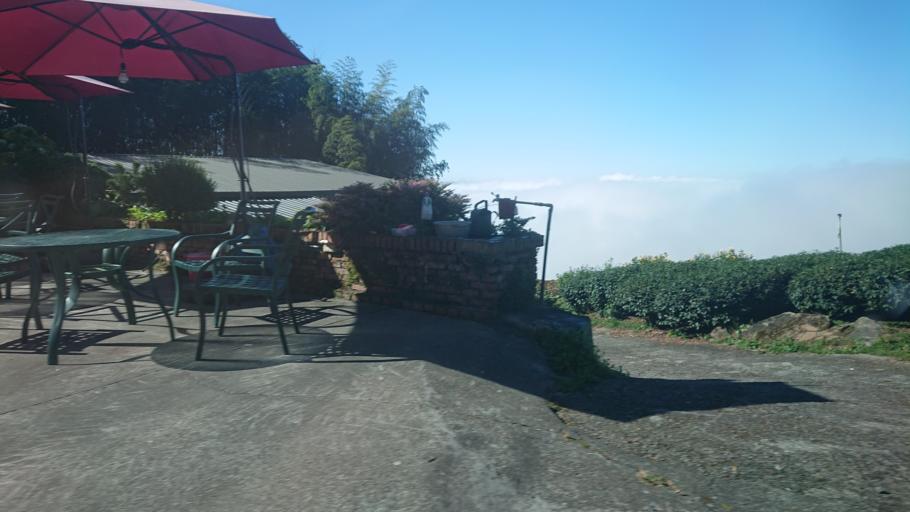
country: TW
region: Taiwan
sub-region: Chiayi
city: Jiayi Shi
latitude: 23.4784
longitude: 120.7007
